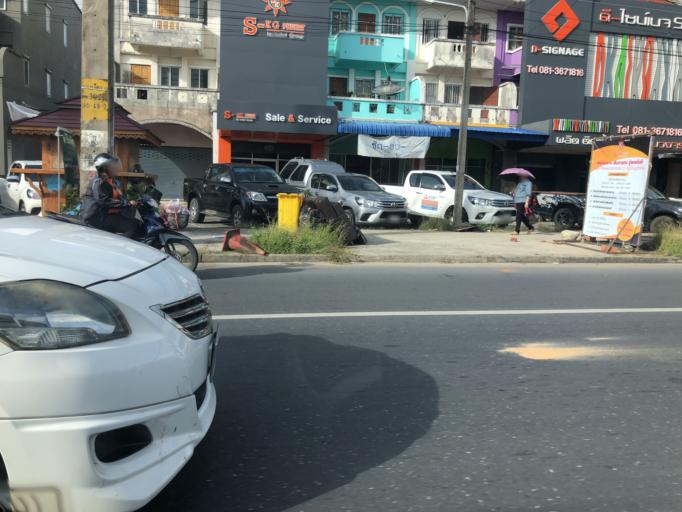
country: TH
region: Phuket
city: Thalang
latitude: 7.9844
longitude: 98.3605
